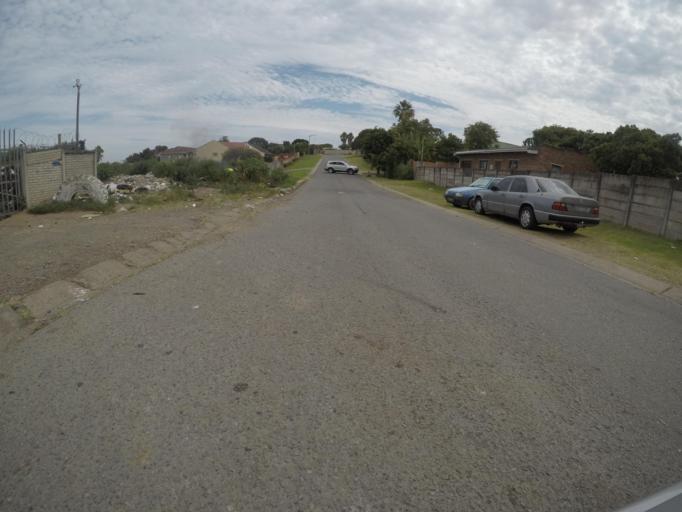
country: ZA
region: Eastern Cape
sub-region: Buffalo City Metropolitan Municipality
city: East London
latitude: -32.9959
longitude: 27.8712
